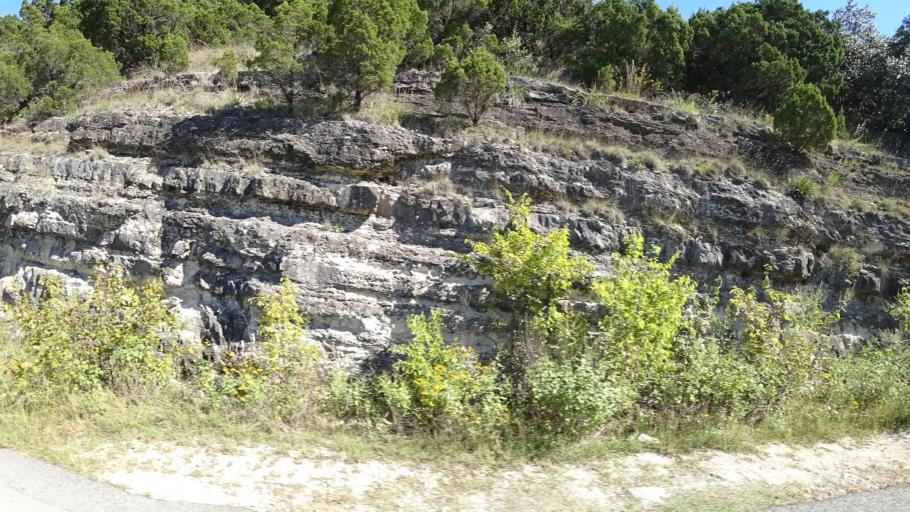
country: US
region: Texas
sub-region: Travis County
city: West Lake Hills
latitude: 30.3243
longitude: -97.7738
